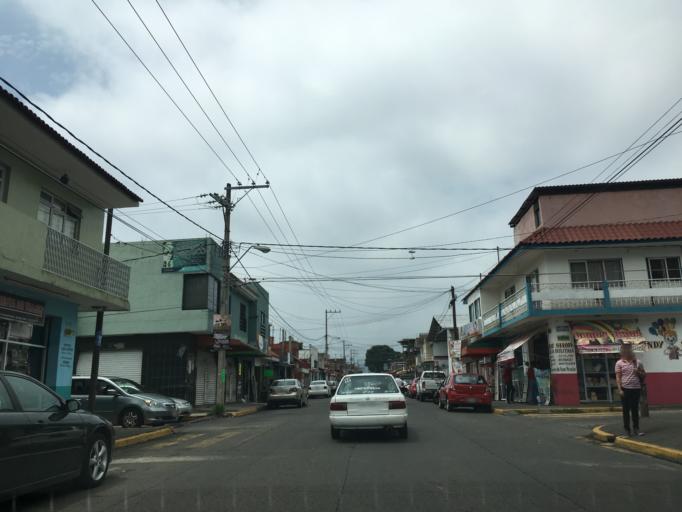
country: MX
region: Michoacan
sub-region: Uruapan
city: Uruapan
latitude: 19.4198
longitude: -102.0499
